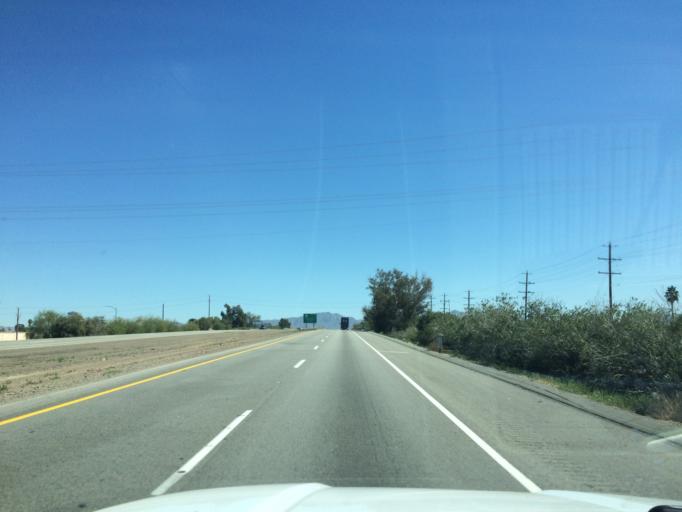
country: US
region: California
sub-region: Riverside County
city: Blythe
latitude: 33.6070
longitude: -114.5910
